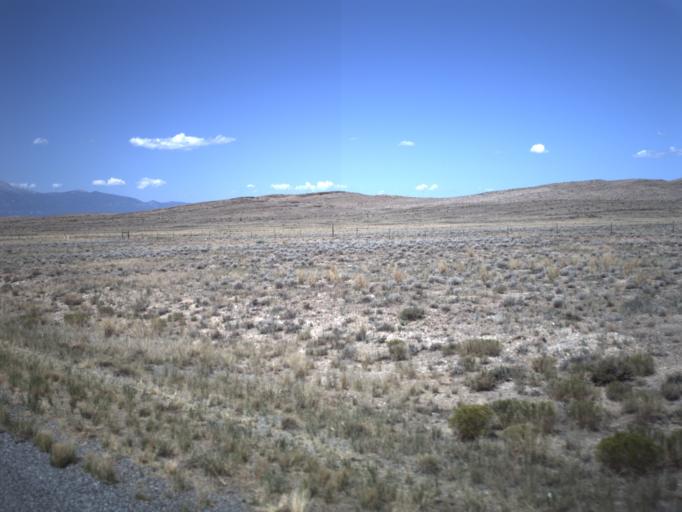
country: US
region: Utah
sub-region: Beaver County
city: Milford
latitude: 39.0447
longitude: -113.8007
